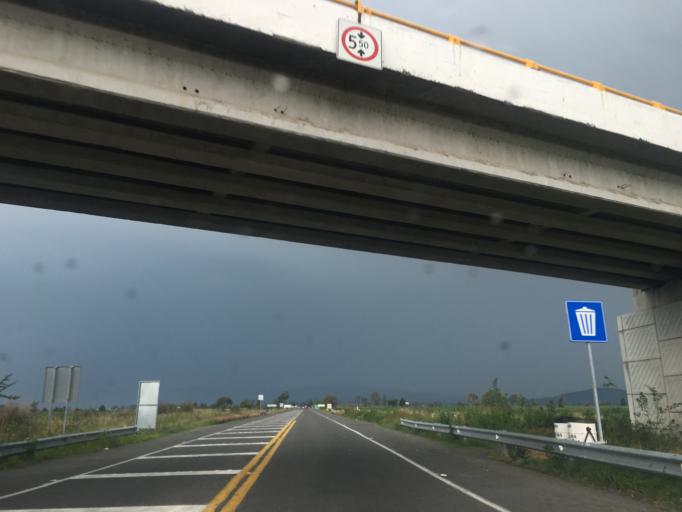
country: MX
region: Michoacan
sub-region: Alvaro Obregon
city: Lazaro Cardenas (La Purisima)
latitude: 19.8847
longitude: -101.0099
